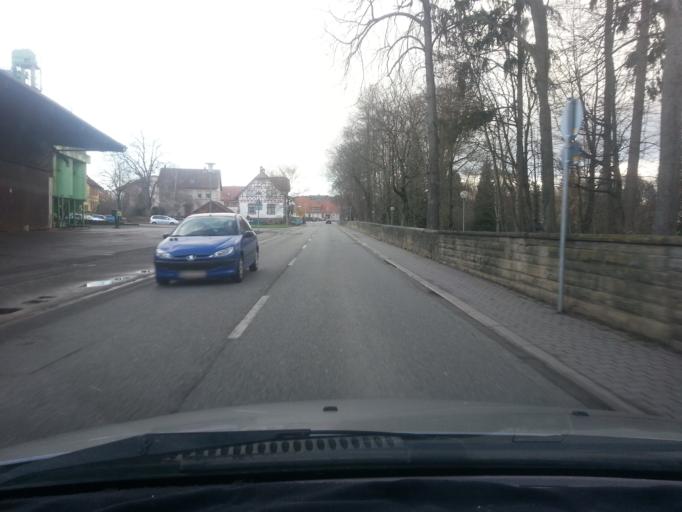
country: DE
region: Baden-Wuerttemberg
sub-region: Karlsruhe Region
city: Balzfeld
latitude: 49.2323
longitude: 8.7752
